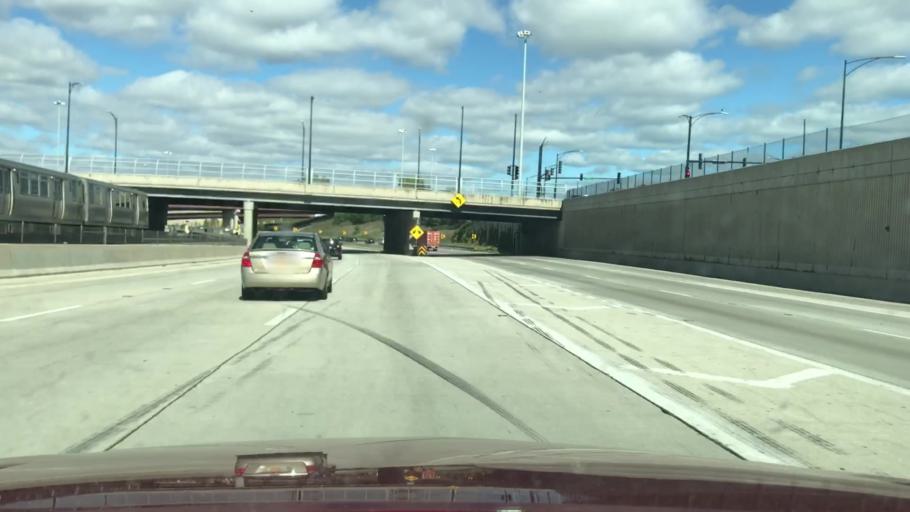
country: US
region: Illinois
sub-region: Cook County
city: Chicago
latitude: 41.7717
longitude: -87.6256
